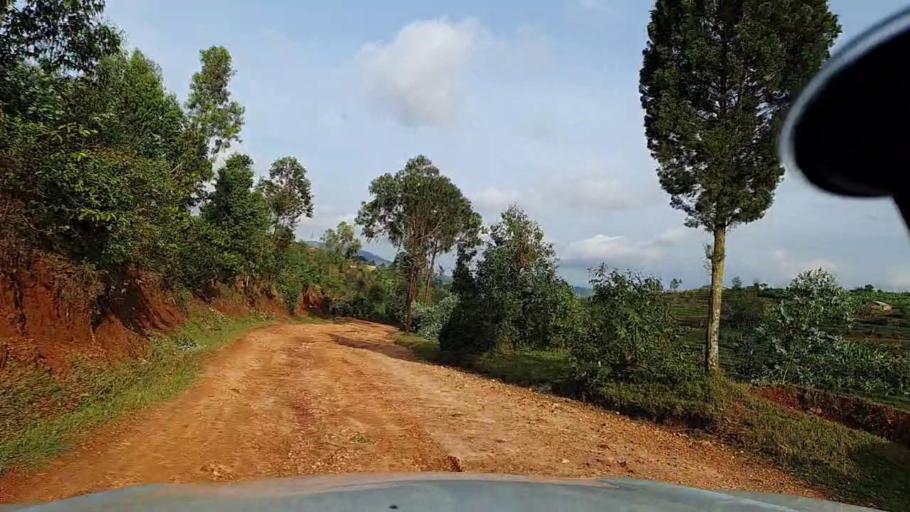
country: RW
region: Southern Province
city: Gitarama
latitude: -2.1863
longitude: 29.5665
